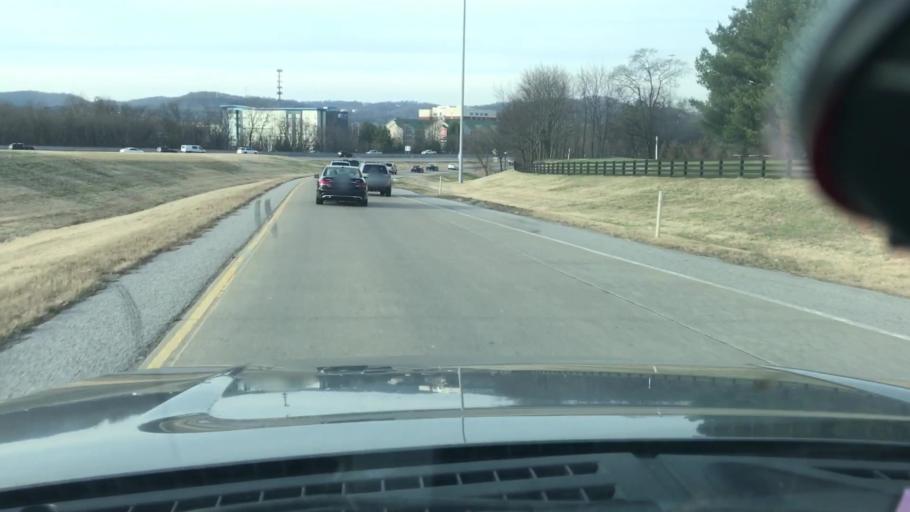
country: US
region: Tennessee
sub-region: Williamson County
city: Franklin
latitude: 35.9489
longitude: -86.8117
